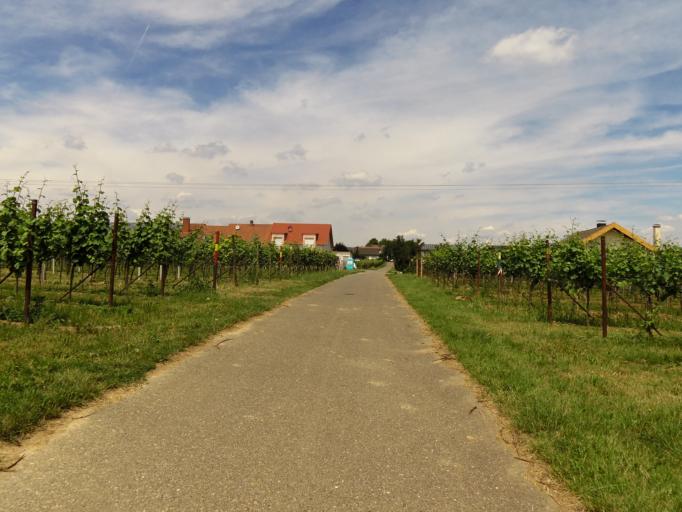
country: DE
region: Rheinland-Pfalz
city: Landau in der Pfalz
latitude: 49.2187
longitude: 8.1076
